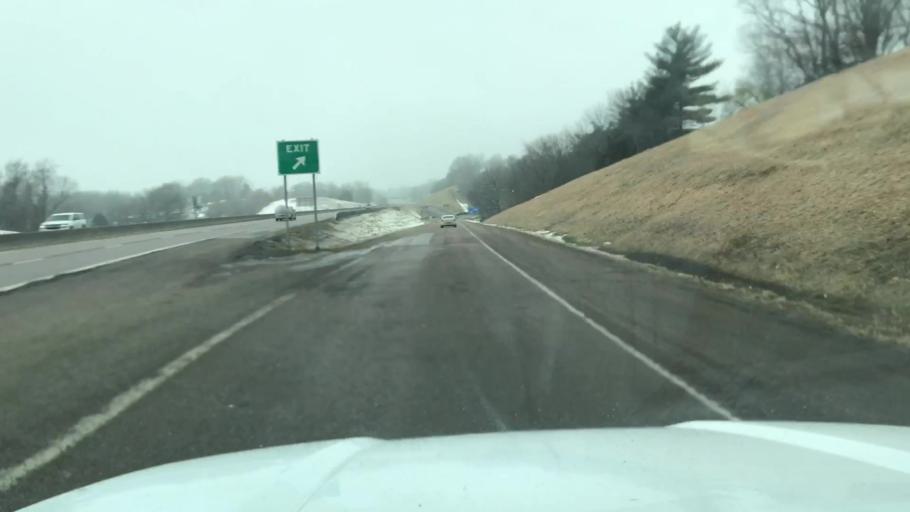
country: US
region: Missouri
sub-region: Buchanan County
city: Saint Joseph
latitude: 39.7469
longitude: -94.7976
